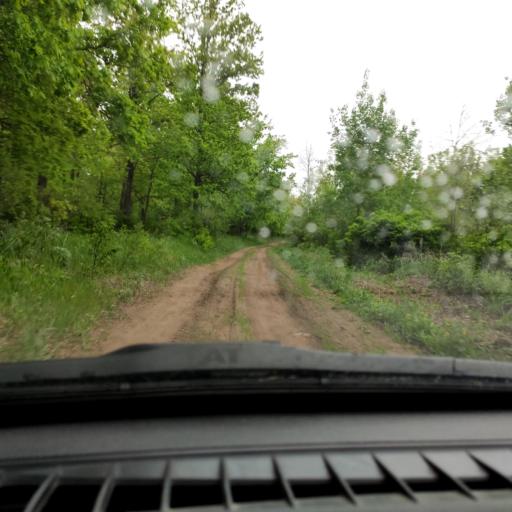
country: RU
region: Samara
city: Zhigulevsk
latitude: 53.5199
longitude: 49.5533
